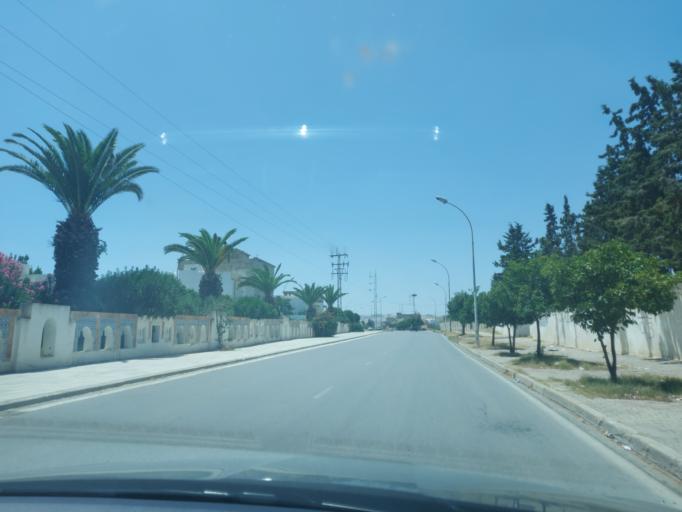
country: TN
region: Silyanah
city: Siliana
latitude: 36.0853
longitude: 9.3596
